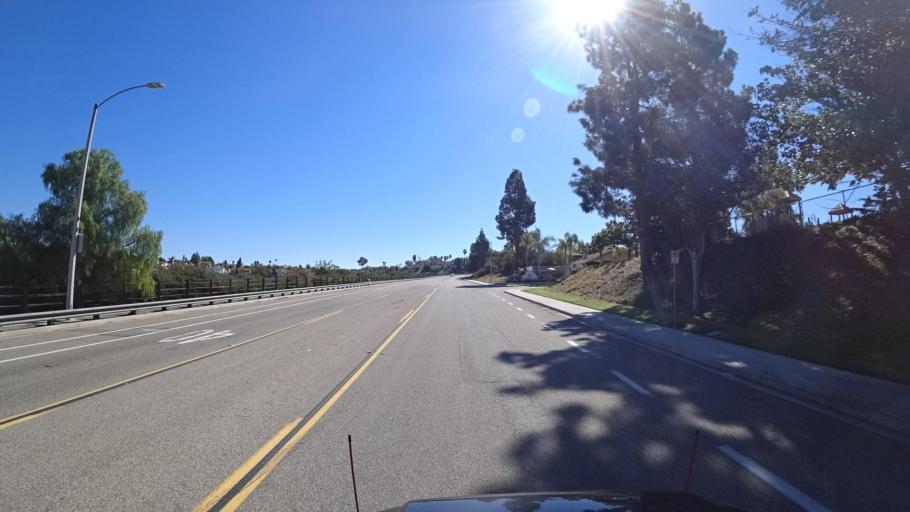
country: US
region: California
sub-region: San Diego County
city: Bonita
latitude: 32.6577
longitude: -116.9939
